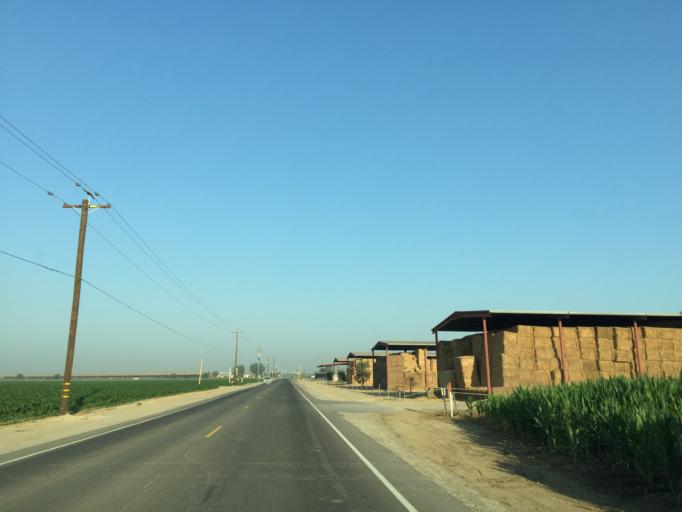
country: US
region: California
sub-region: Tulare County
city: London
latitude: 36.4585
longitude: -119.3885
